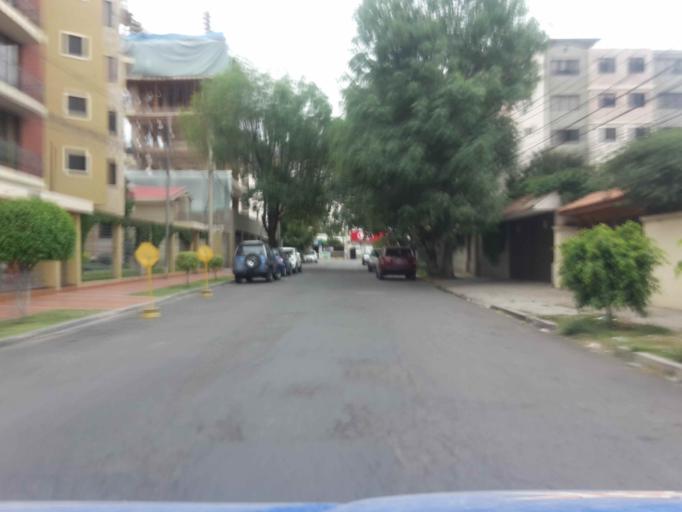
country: BO
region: Cochabamba
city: Cochabamba
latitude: -17.3760
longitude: -66.1554
